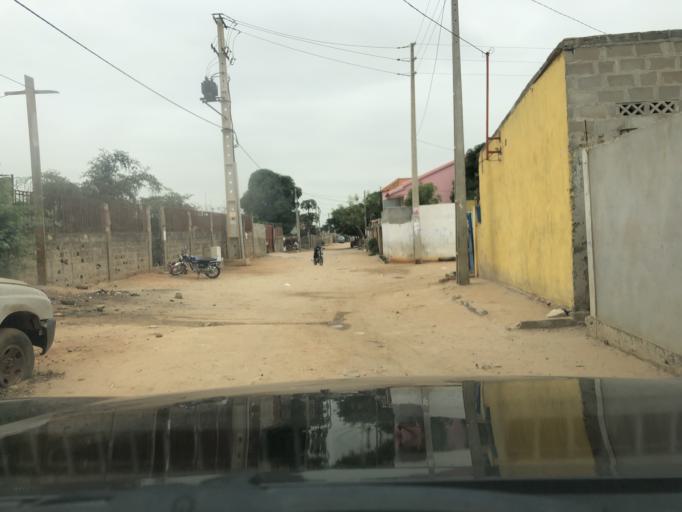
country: AO
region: Luanda
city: Luanda
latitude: -8.9376
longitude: 13.2339
